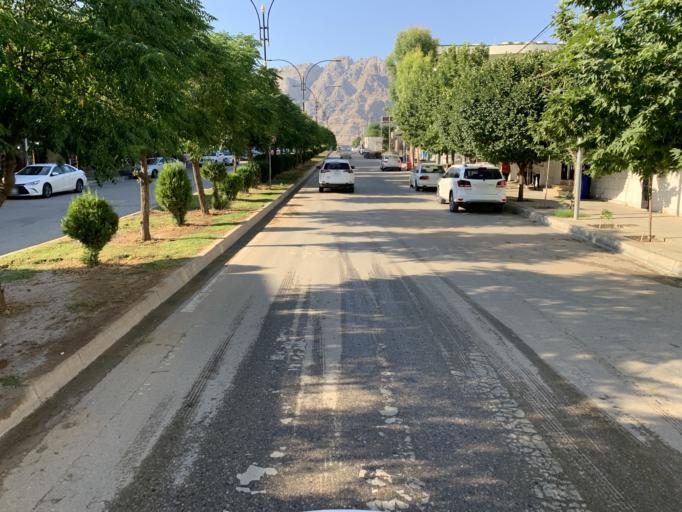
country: IQ
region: As Sulaymaniyah
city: Raniye
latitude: 36.2473
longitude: 44.8753
